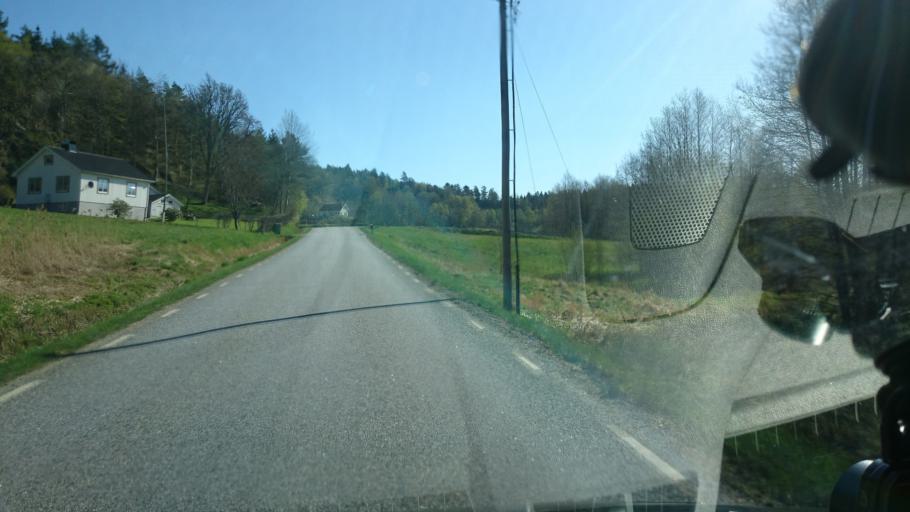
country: SE
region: Vaestra Goetaland
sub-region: Munkedals Kommun
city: Munkedal
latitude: 58.4141
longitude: 11.6796
